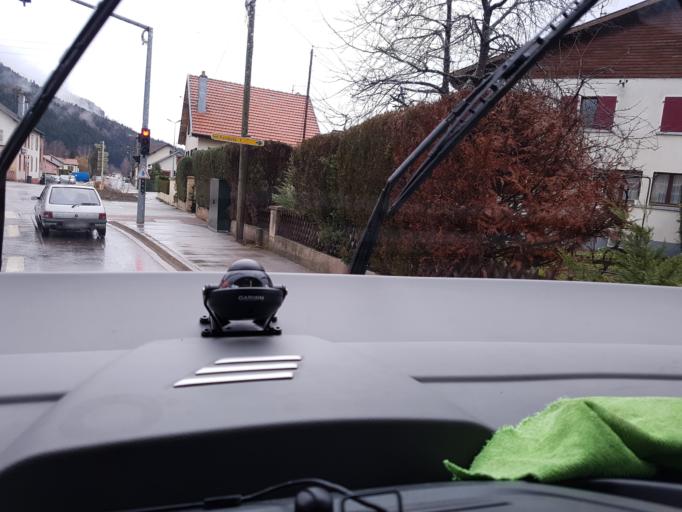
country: FR
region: Lorraine
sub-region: Departement des Vosges
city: Saint-Die-des-Vosges
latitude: 48.2887
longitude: 6.9269
